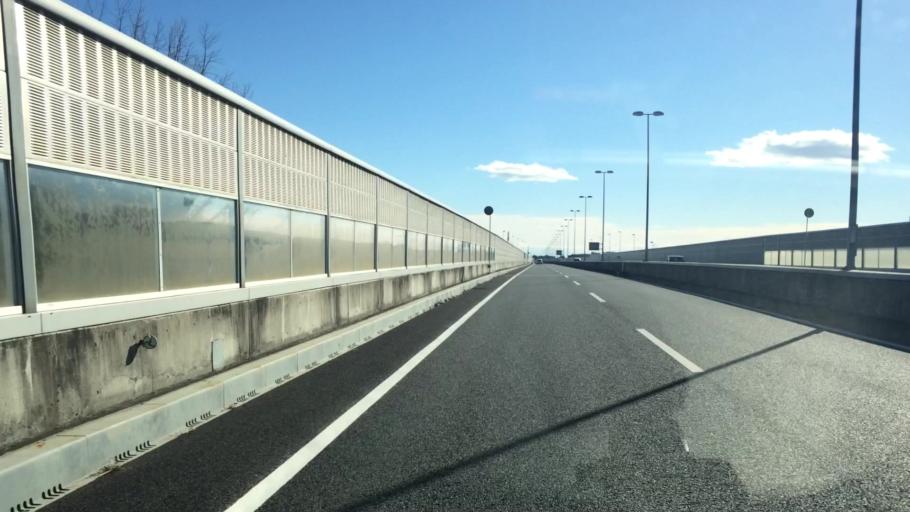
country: JP
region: Tochigi
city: Utsunomiya-shi
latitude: 36.6145
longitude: 139.8590
